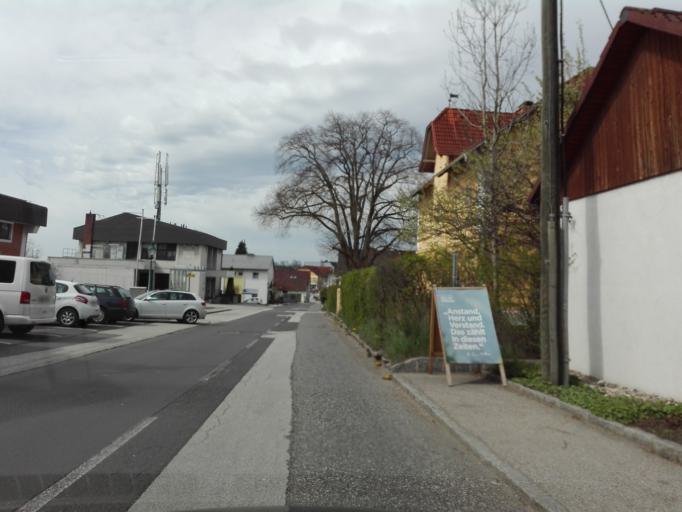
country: AT
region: Upper Austria
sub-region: Politischer Bezirk Urfahr-Umgebung
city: Gramastetten
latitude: 48.3808
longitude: 14.1941
